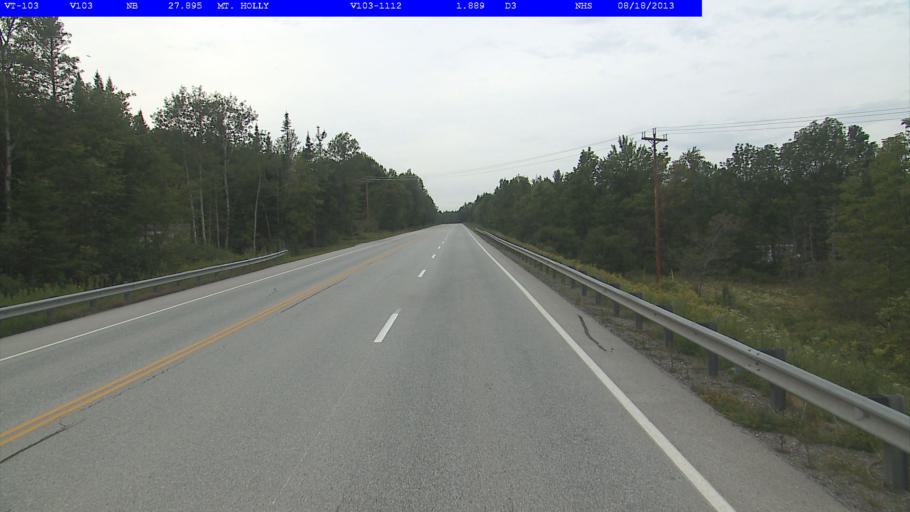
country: US
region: Vermont
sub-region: Windsor County
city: Chester
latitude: 43.4426
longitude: -72.7676
